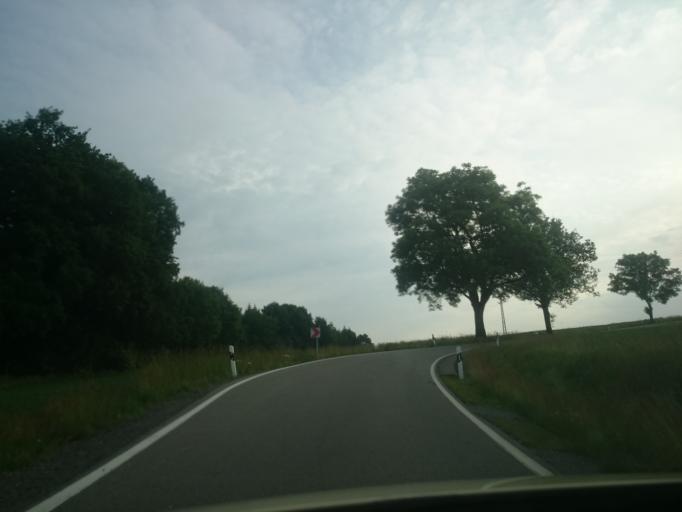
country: DE
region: Saxony
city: Oberschona
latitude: 50.8637
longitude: 13.2492
